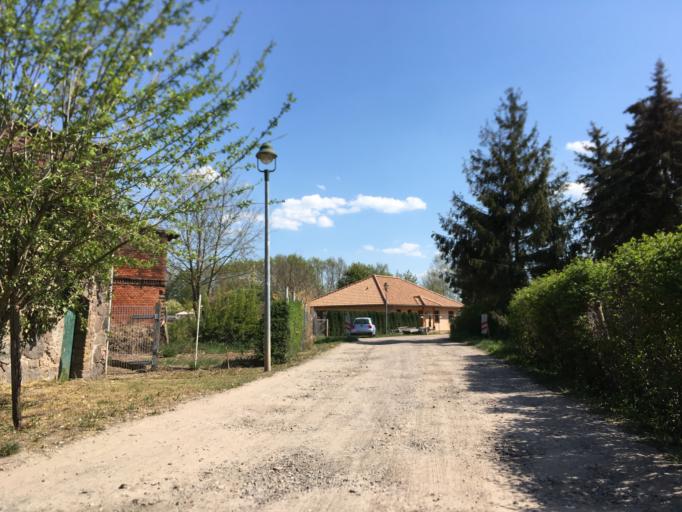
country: DE
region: Brandenburg
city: Werneuchen
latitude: 52.6220
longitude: 13.6832
